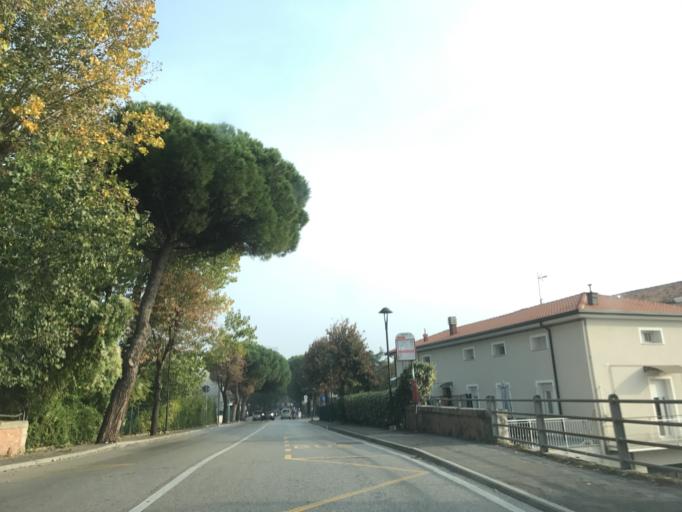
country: IT
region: Emilia-Romagna
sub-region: Provincia di Rimini
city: Rimini
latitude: 44.0724
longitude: 12.5617
